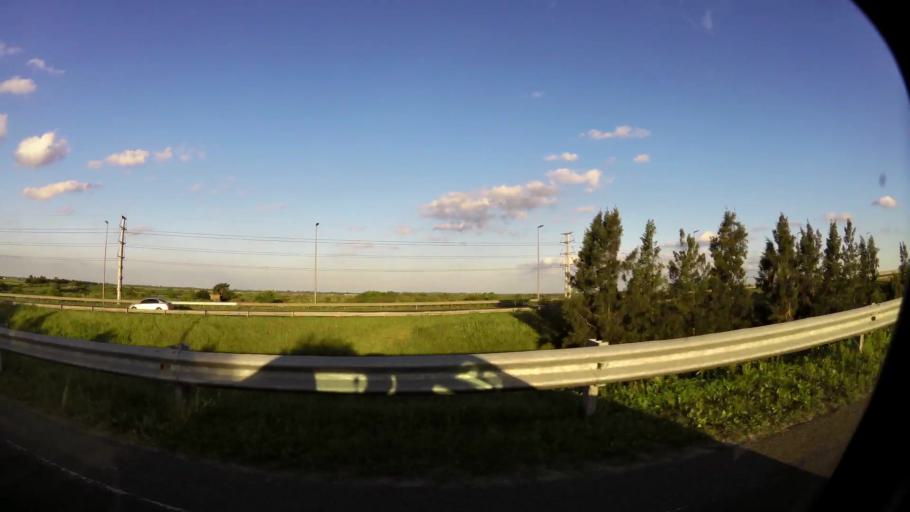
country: AR
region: Buenos Aires
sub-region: Partido de Quilmes
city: Quilmes
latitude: -34.7817
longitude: -58.1522
